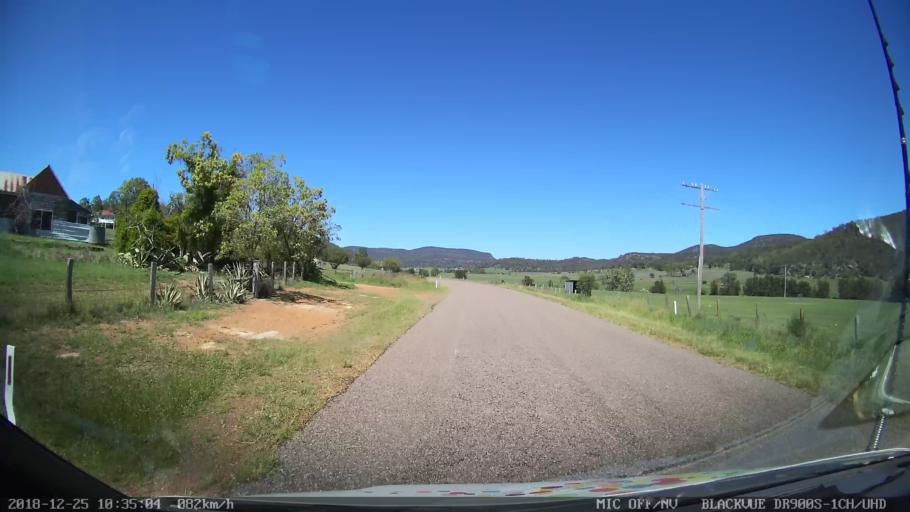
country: AU
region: New South Wales
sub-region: Upper Hunter Shire
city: Merriwa
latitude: -32.3952
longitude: 150.3995
